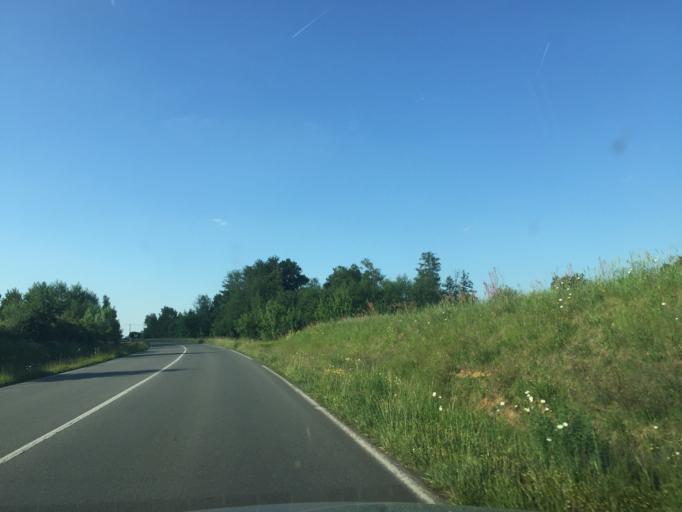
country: FR
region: Aquitaine
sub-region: Departement de la Dordogne
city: La Roche-Chalais
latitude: 45.1871
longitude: 0.0292
